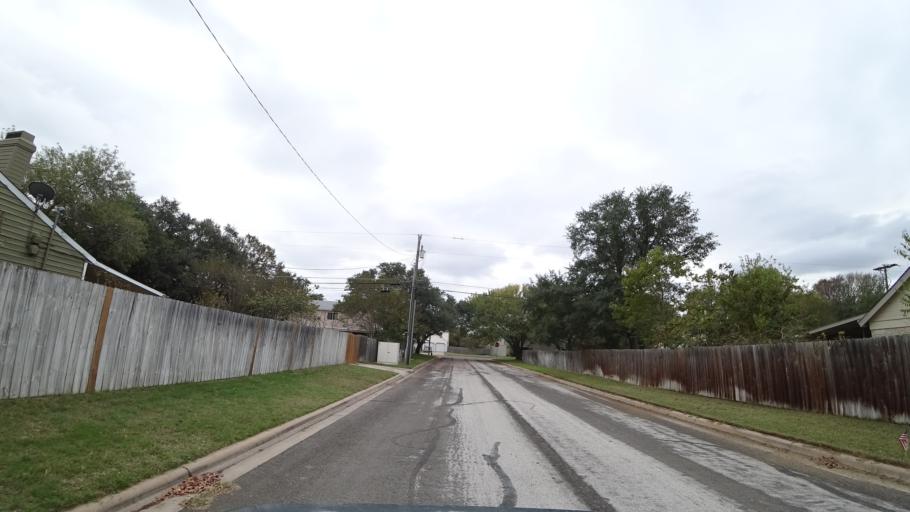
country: US
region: Texas
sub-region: Williamson County
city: Round Rock
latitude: 30.4915
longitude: -97.7003
